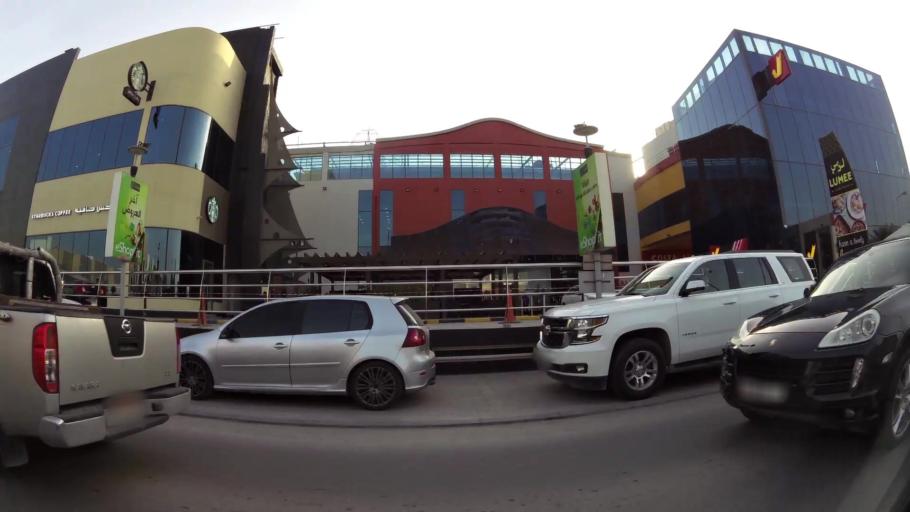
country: BH
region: Manama
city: Jidd Hafs
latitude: 26.2006
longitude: 50.4982
